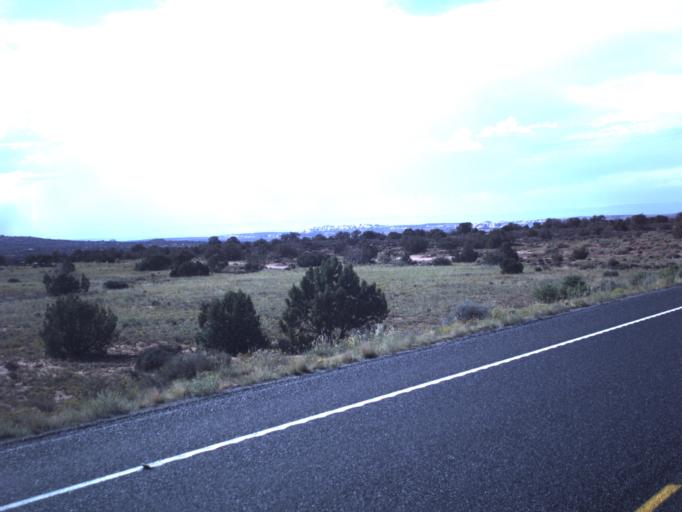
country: US
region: Utah
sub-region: Grand County
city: Moab
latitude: 38.5999
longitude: -109.8146
